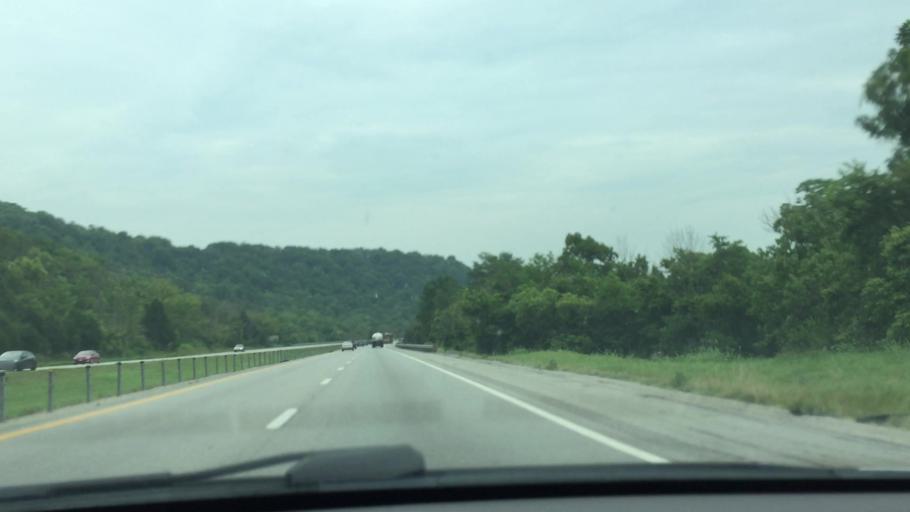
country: US
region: Kentucky
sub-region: Carroll County
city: Carrollton
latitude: 38.6200
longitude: -85.1575
